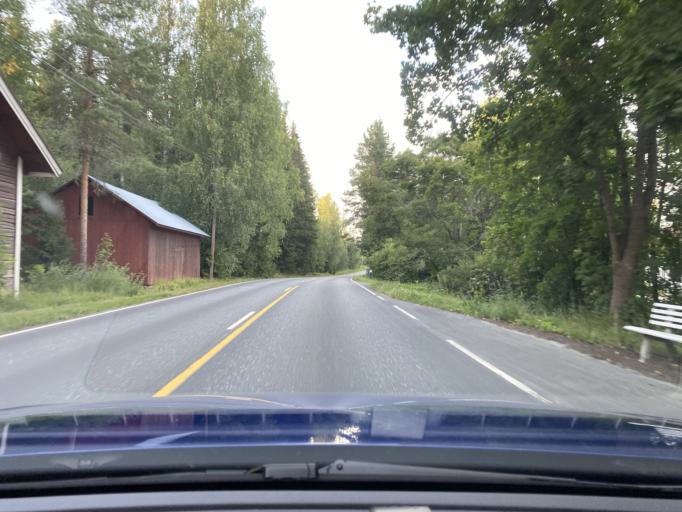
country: FI
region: Pirkanmaa
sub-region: Lounais-Pirkanmaa
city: Punkalaidun
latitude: 61.1946
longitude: 23.0343
